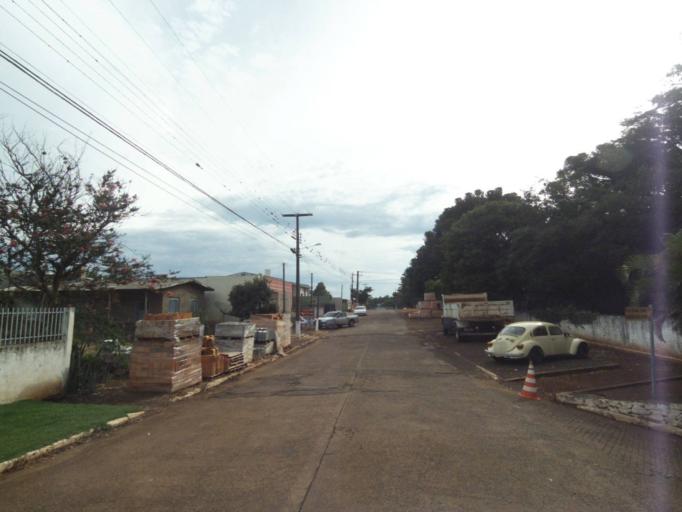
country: BR
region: Parana
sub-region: Guaraniacu
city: Guaraniacu
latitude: -25.1022
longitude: -52.8775
